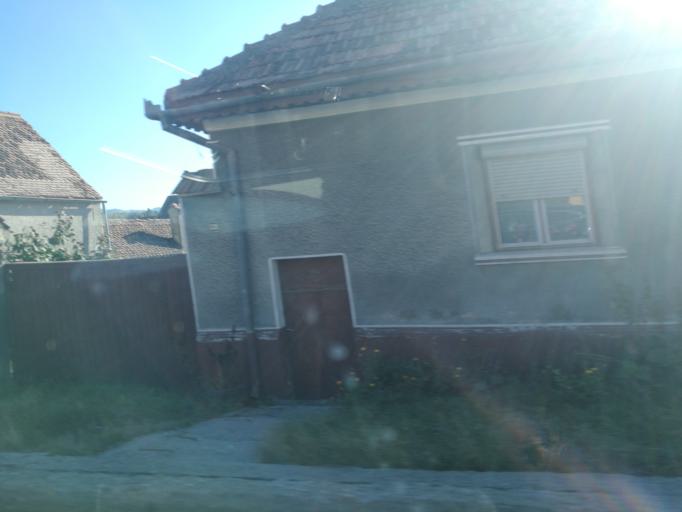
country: RO
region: Brasov
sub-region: Comuna Dumbravita
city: Dumbravita
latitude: 45.7668
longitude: 25.3683
